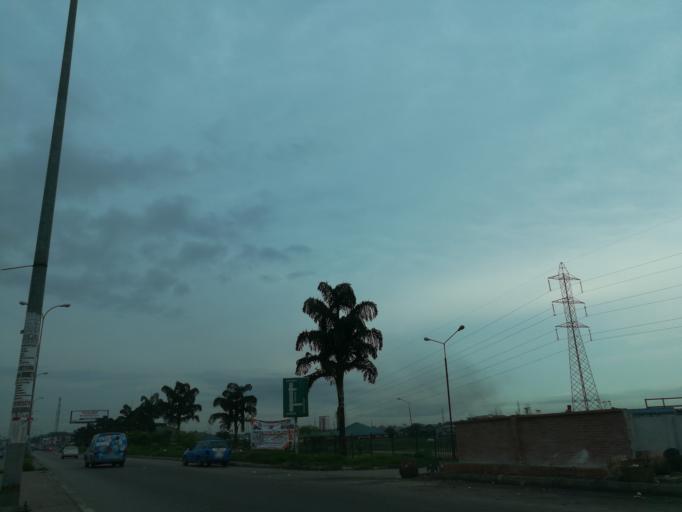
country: NG
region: Rivers
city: Port Harcourt
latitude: 4.8254
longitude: 7.0249
